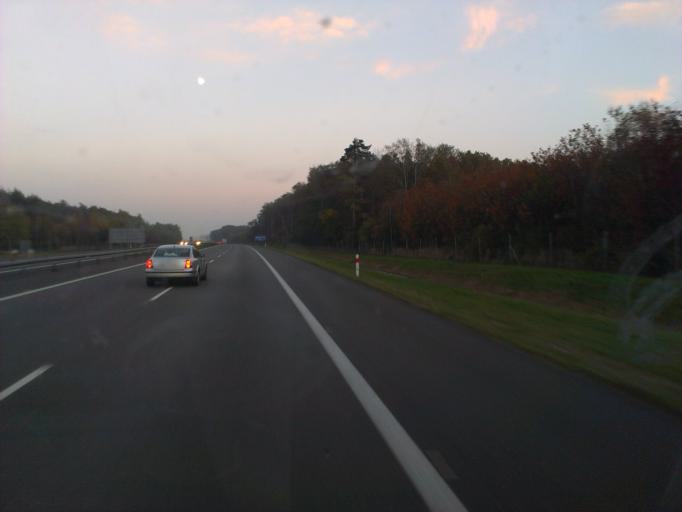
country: PL
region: Opole Voivodeship
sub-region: Powiat strzelecki
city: Strzelce Opolskie
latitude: 50.4545
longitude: 18.2954
